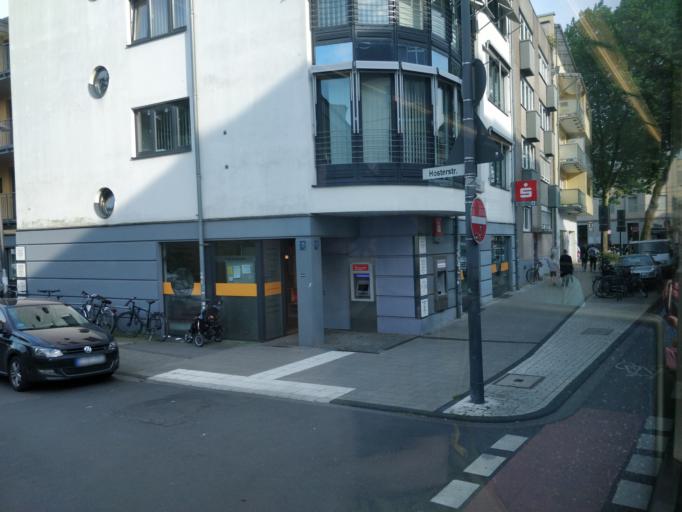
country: DE
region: North Rhine-Westphalia
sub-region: Regierungsbezirk Koln
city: Bilderstoeckchen
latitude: 50.9589
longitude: 6.9184
